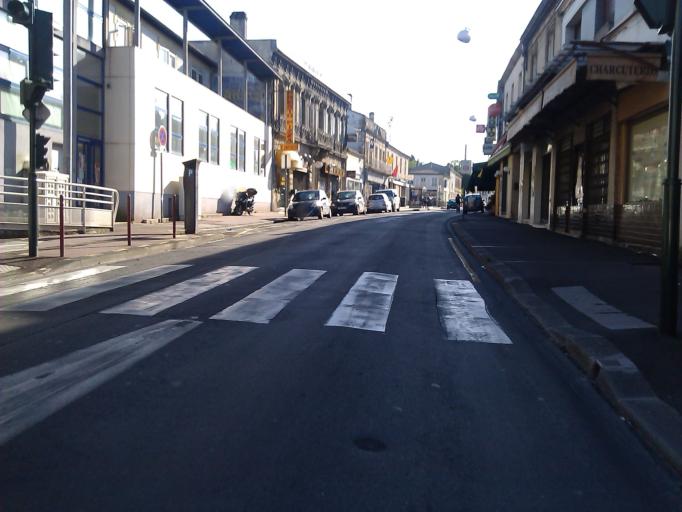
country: FR
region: Aquitaine
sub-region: Departement de la Gironde
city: Pessac
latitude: 44.8064
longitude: -0.6297
